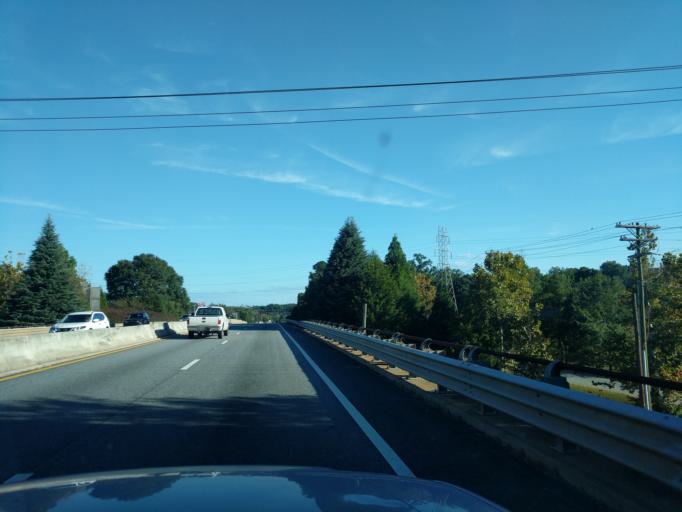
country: US
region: South Carolina
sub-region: Spartanburg County
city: Spartanburg
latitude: 34.9730
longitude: -81.9390
